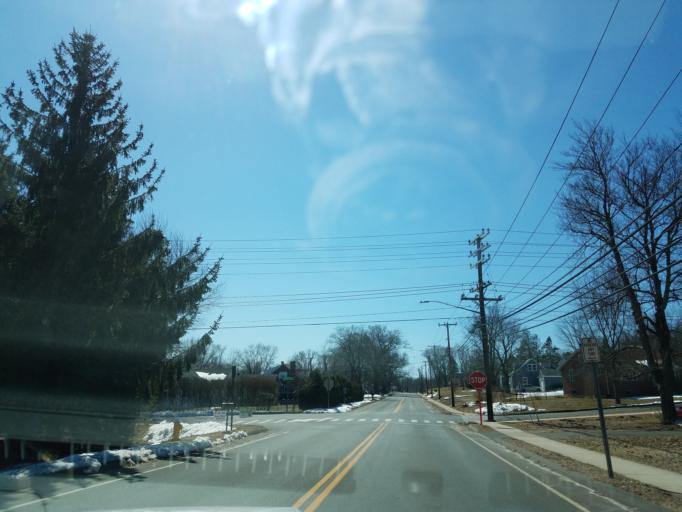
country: US
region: Connecticut
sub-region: Hartford County
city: Windsor Locks
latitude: 41.9201
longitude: -72.6342
